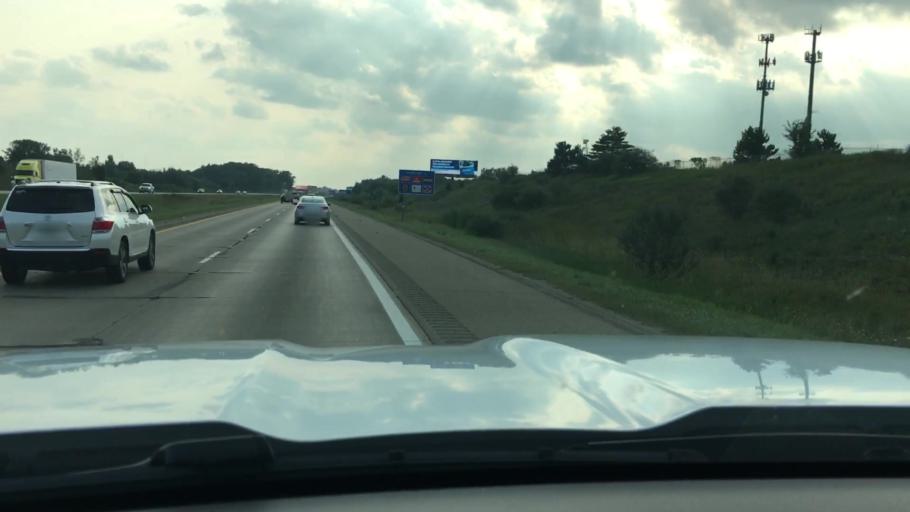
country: US
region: Michigan
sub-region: Kent County
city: Kentwood
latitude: 42.8508
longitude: -85.6039
